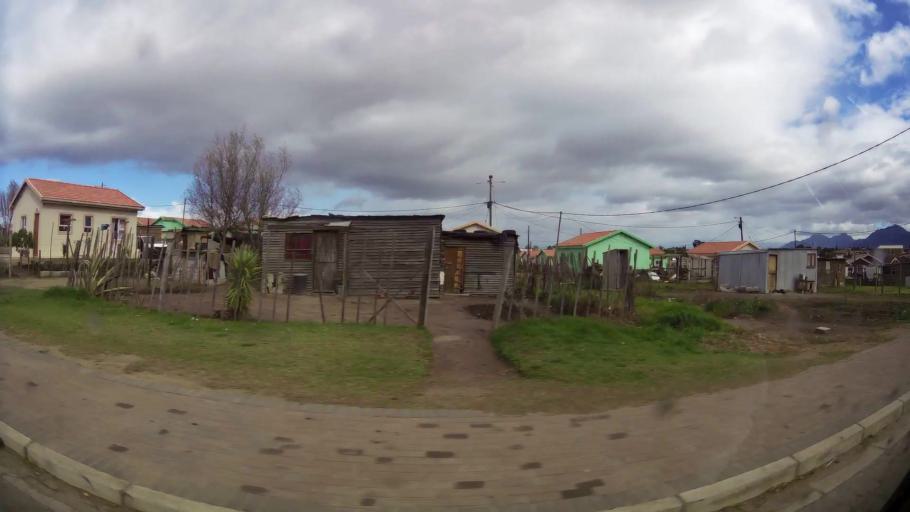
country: ZA
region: Western Cape
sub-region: Eden District Municipality
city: George
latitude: -33.9746
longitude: 22.4891
